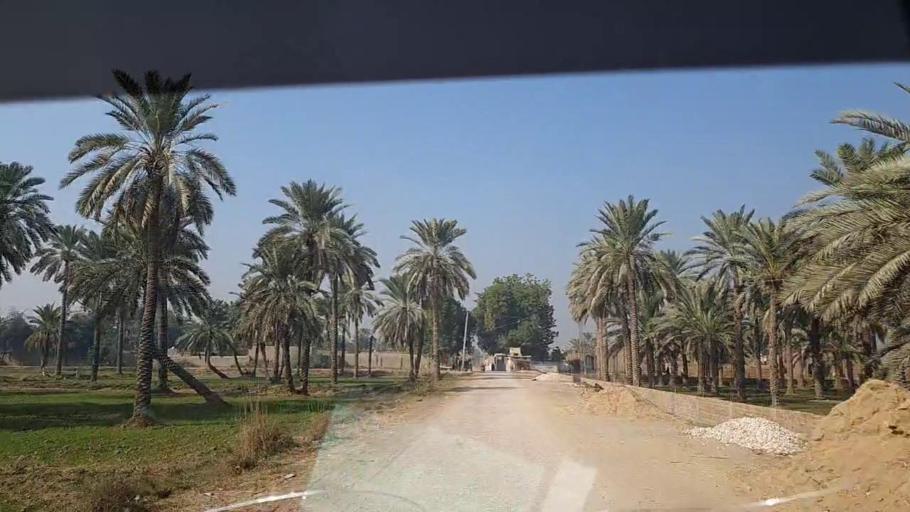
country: PK
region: Sindh
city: Khairpur
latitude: 27.4917
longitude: 68.7556
